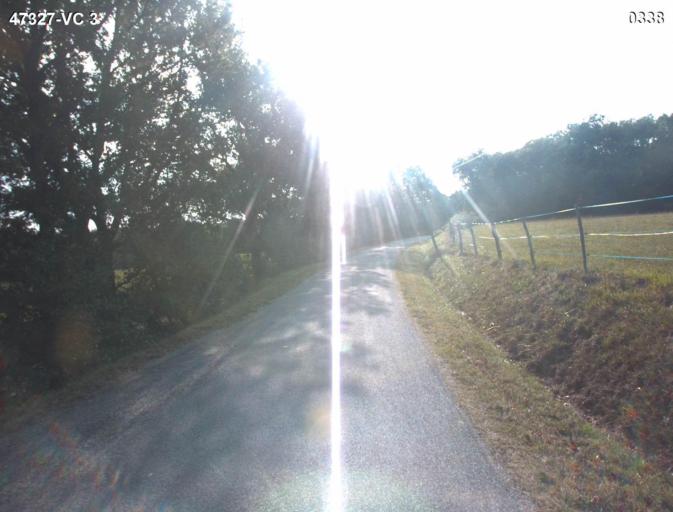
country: FR
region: Aquitaine
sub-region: Departement du Lot-et-Garonne
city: Barbaste
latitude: 44.2064
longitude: 0.2391
